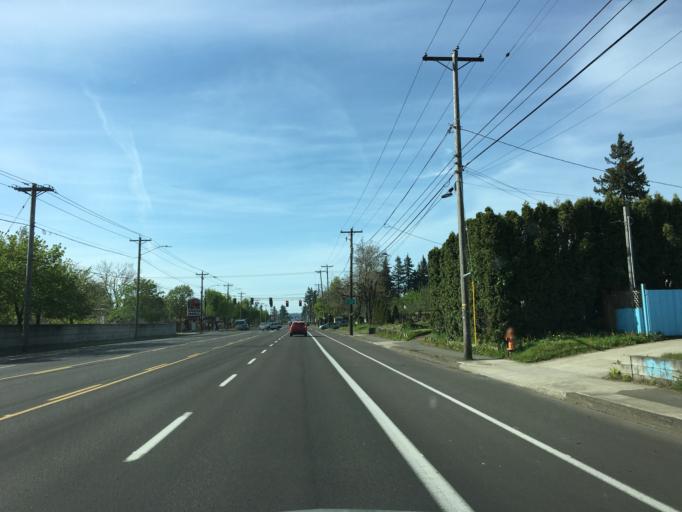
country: US
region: Oregon
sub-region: Multnomah County
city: Lents
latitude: 45.5385
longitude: -122.5377
